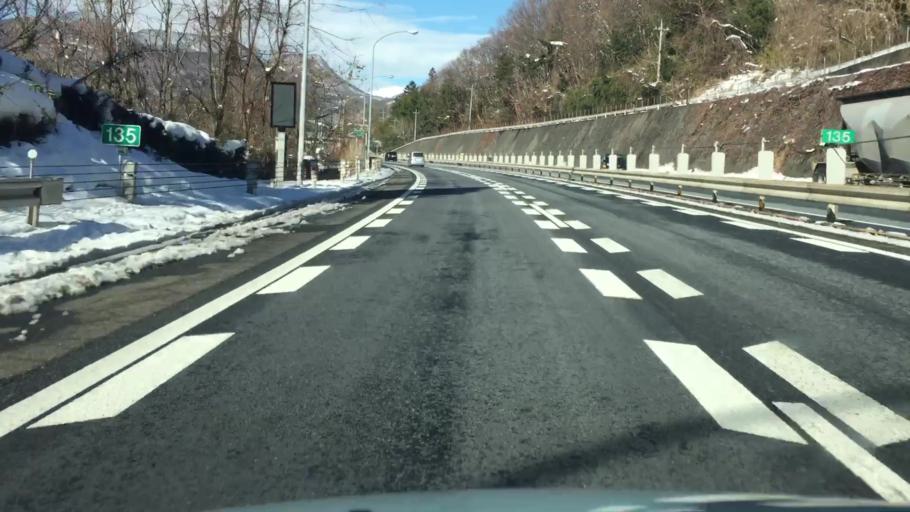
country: JP
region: Gunma
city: Numata
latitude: 36.6977
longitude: 138.9910
